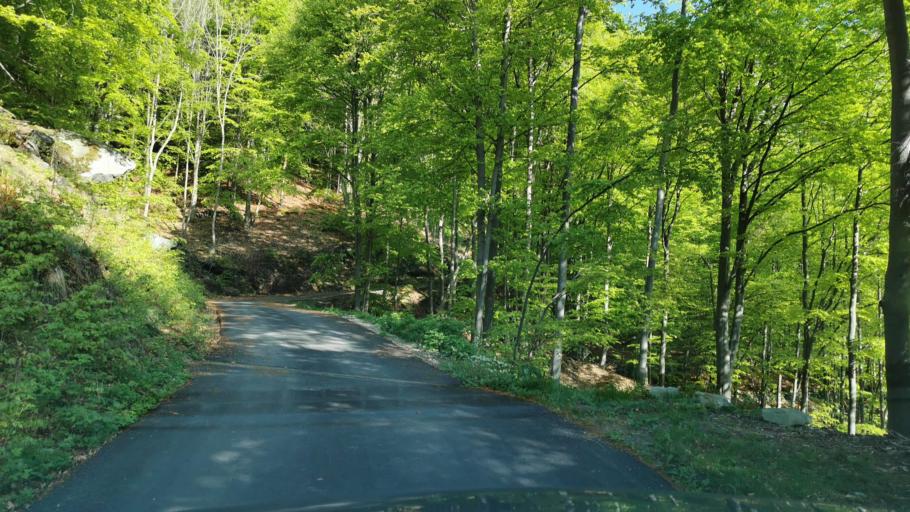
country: IT
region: Piedmont
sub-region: Provincia di Torino
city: Lemie
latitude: 45.2403
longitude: 7.2809
